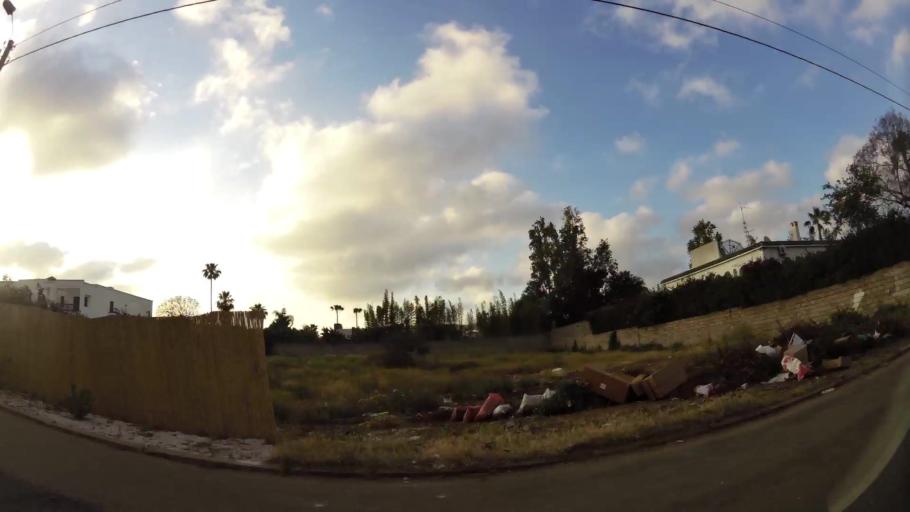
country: MA
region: Rabat-Sale-Zemmour-Zaer
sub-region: Rabat
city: Rabat
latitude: 33.9591
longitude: -6.8299
